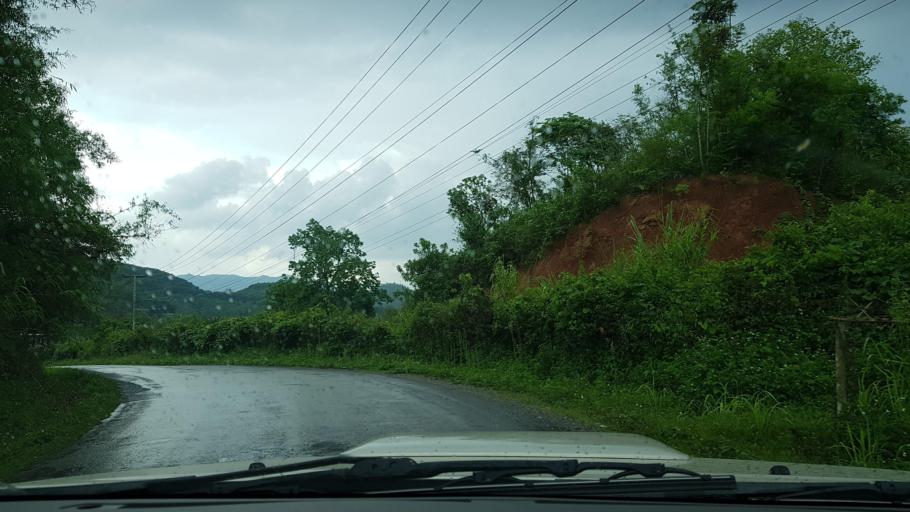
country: LA
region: Oudomxai
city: Muang Xay
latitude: 20.5674
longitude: 101.9207
